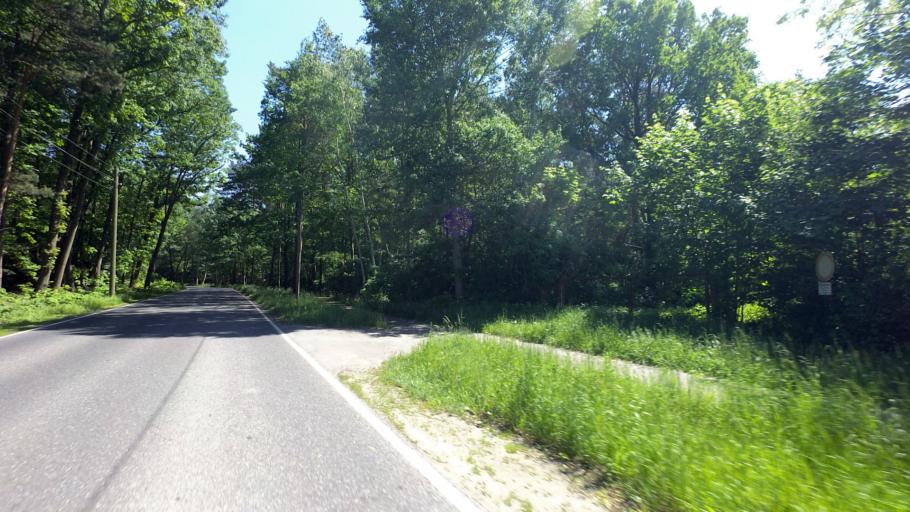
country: DE
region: Brandenburg
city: Cottbus
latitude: 51.7960
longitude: 14.3763
